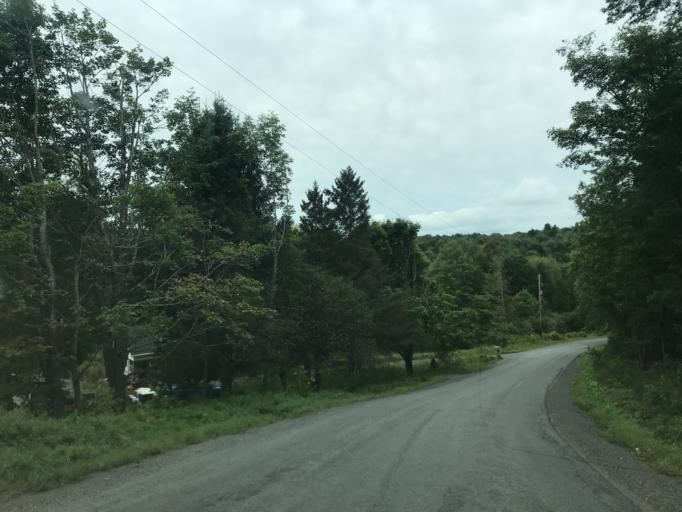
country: US
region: New York
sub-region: Otsego County
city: Worcester
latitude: 42.5349
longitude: -74.6399
